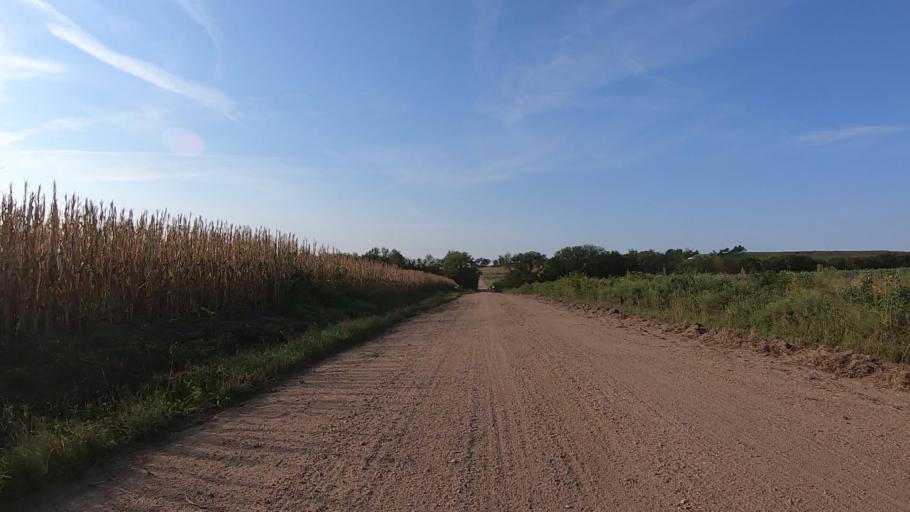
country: US
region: Kansas
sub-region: Marshall County
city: Blue Rapids
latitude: 39.6929
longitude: -96.7792
